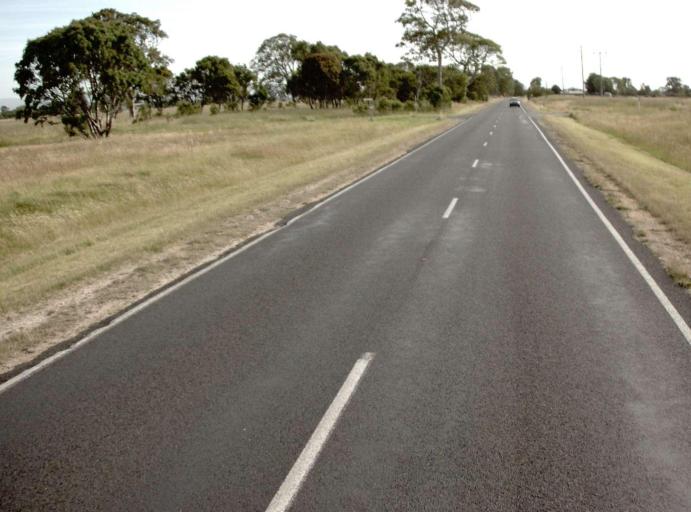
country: AU
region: Victoria
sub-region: Latrobe
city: Traralgon
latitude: -38.0926
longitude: 146.6001
